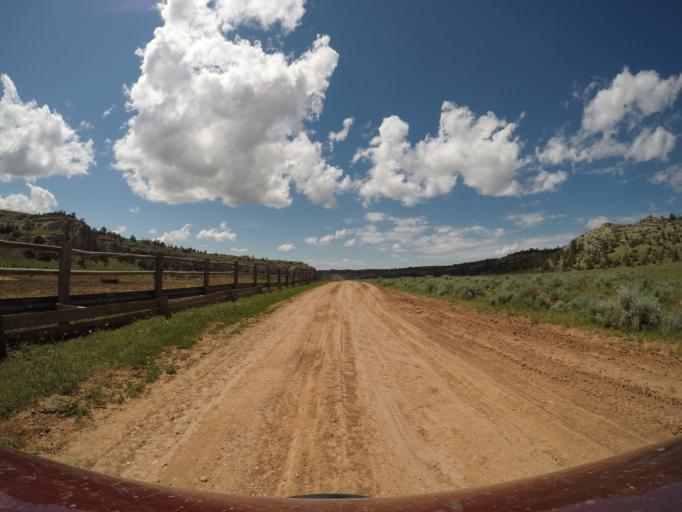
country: US
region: Montana
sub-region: Yellowstone County
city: Laurel
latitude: 45.2392
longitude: -108.6318
